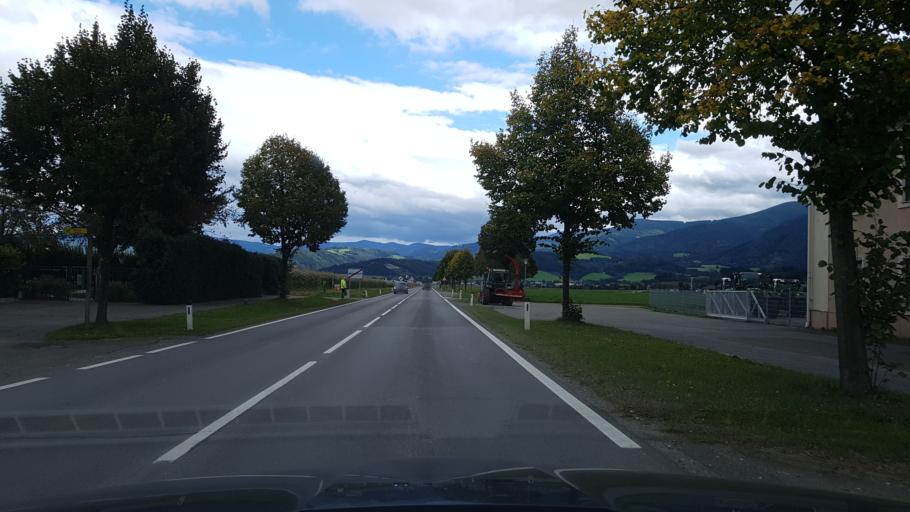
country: AT
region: Styria
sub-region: Politischer Bezirk Murtal
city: Judenburg
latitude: 47.1631
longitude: 14.6998
